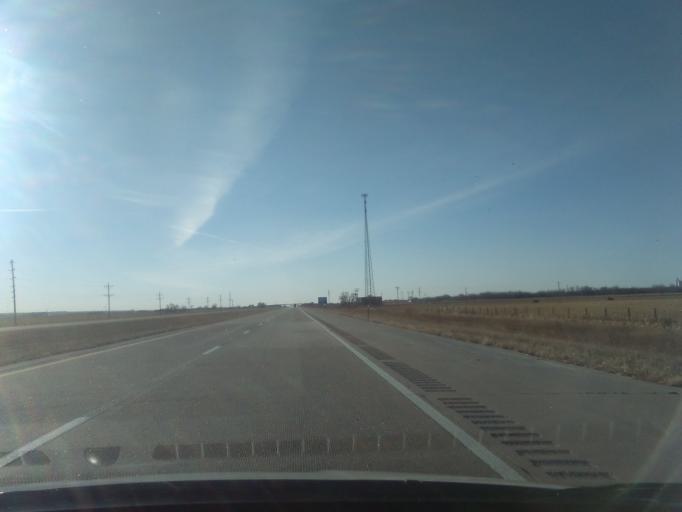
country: US
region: Colorado
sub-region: Sedgwick County
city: Julesburg
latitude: 41.0556
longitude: -102.0489
